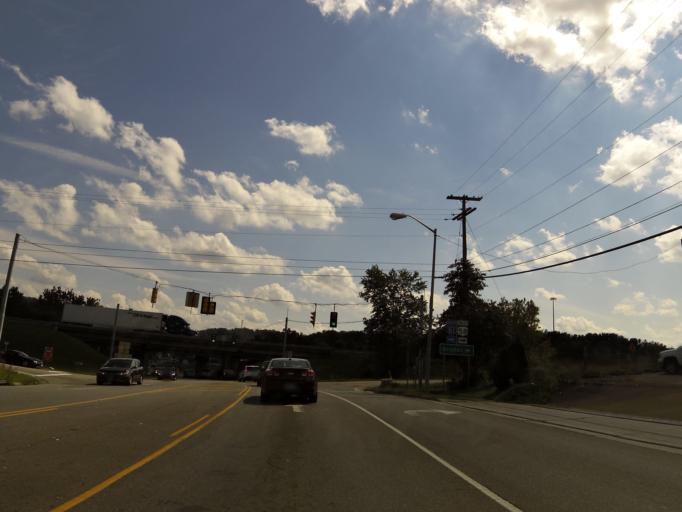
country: US
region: Virginia
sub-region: Washington County
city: Abingdon
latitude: 36.7005
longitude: -81.9747
